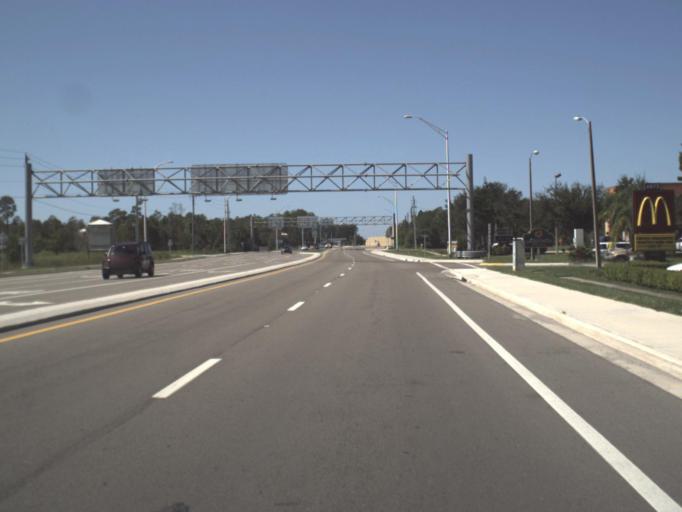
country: US
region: Florida
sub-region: Collier County
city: Golden Gate
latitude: 26.1550
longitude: -81.6879
